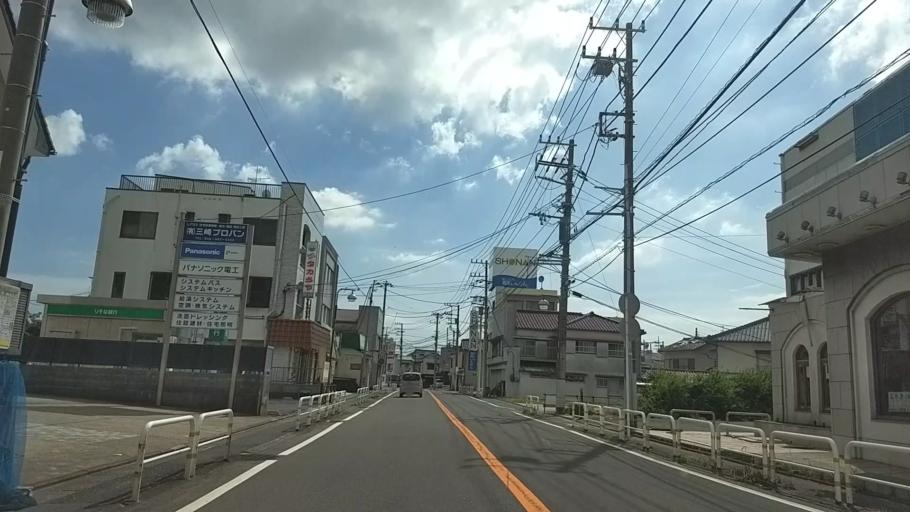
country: JP
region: Kanagawa
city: Miura
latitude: 35.1483
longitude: 139.6264
